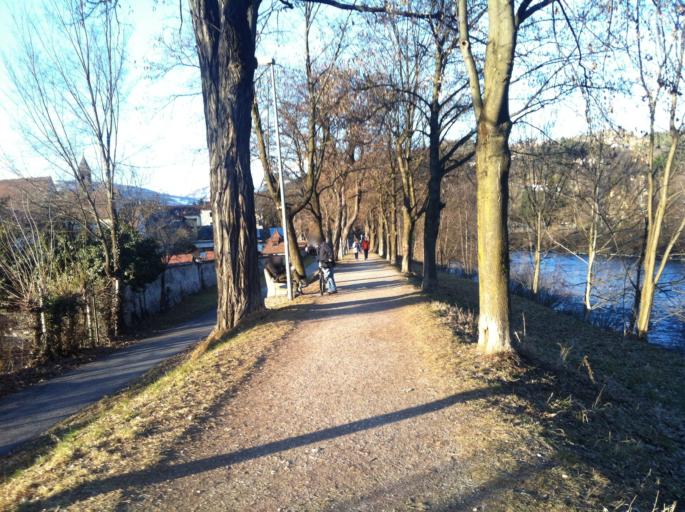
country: IT
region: Trentino-Alto Adige
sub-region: Bolzano
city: Bressanone
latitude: 46.7117
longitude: 11.6599
